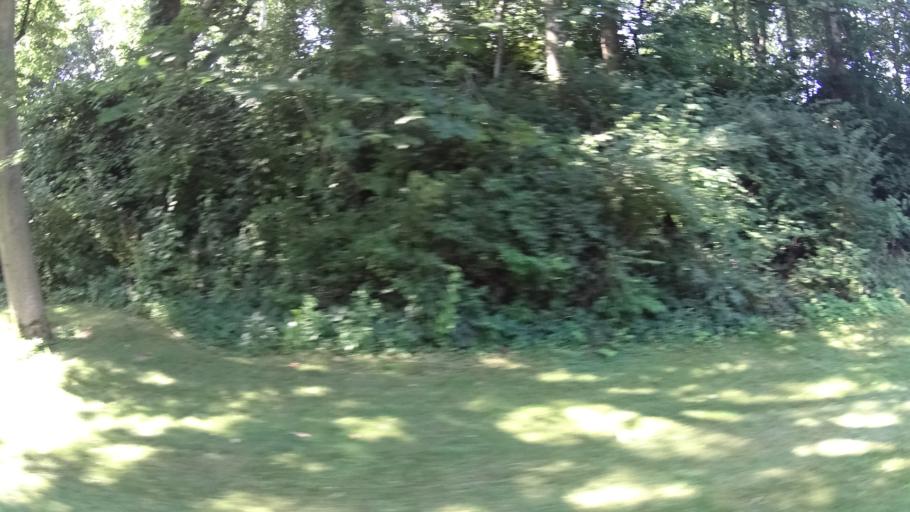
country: US
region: Ohio
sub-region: Huron County
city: Bellevue
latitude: 41.3721
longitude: -82.8359
